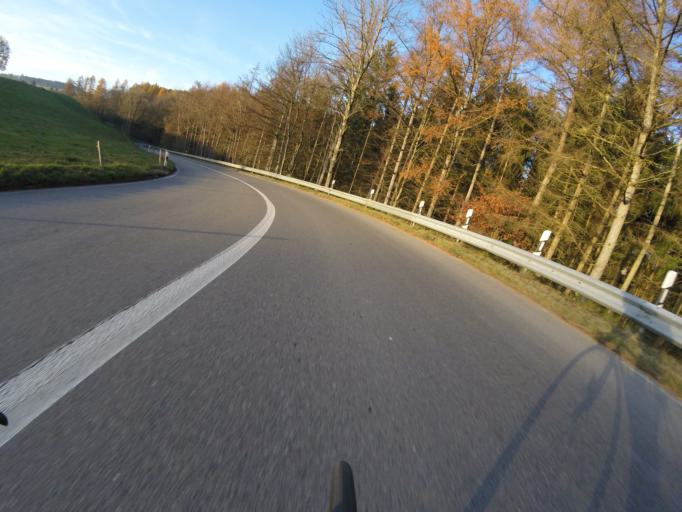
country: CH
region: Bern
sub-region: Bern-Mittelland District
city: Wohlen
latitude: 46.9715
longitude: 7.3476
